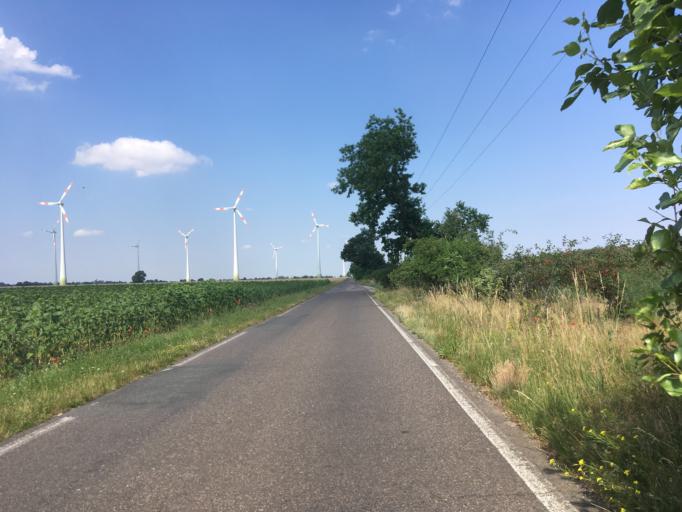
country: DE
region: Saxony-Anhalt
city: Quellendorf
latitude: 51.7828
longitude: 12.1435
